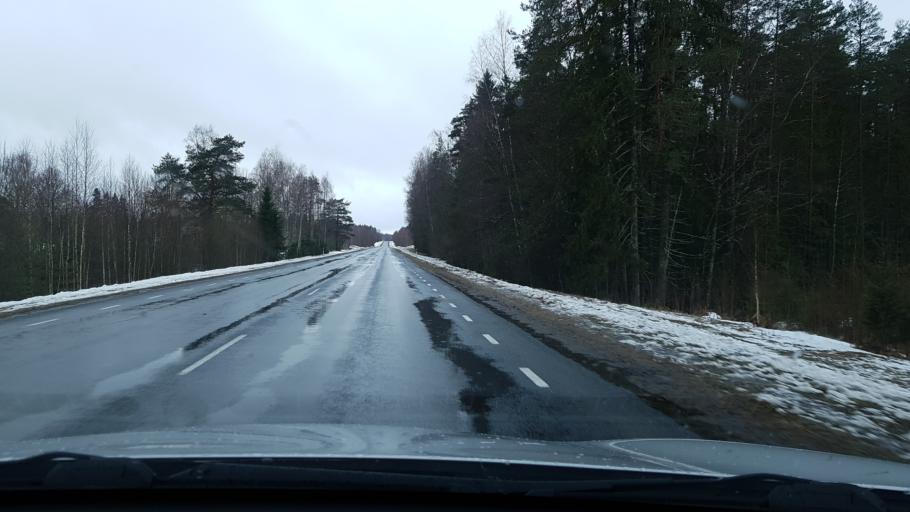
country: LV
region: Apes Novads
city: Ape
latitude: 57.7255
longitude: 26.7771
